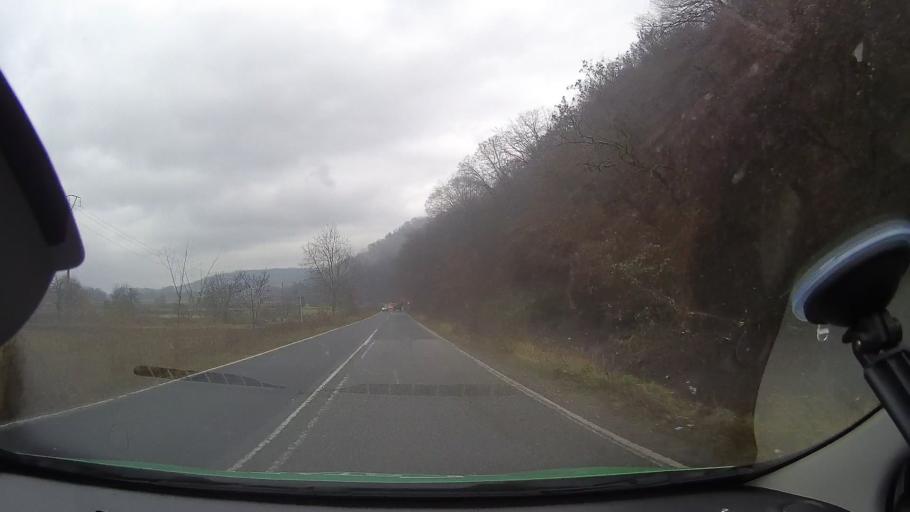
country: RO
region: Arad
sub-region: Comuna Buteni
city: Buteni
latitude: 46.3014
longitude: 22.1620
